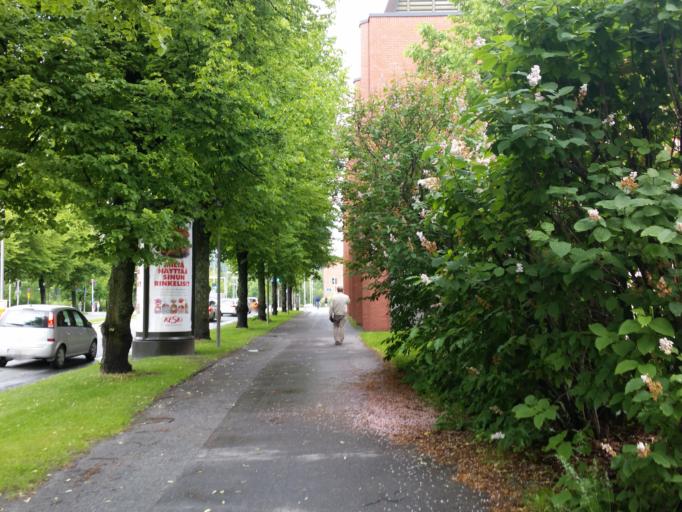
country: FI
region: Northern Savo
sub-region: Kuopio
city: Kuopio
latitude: 62.8937
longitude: 27.6715
